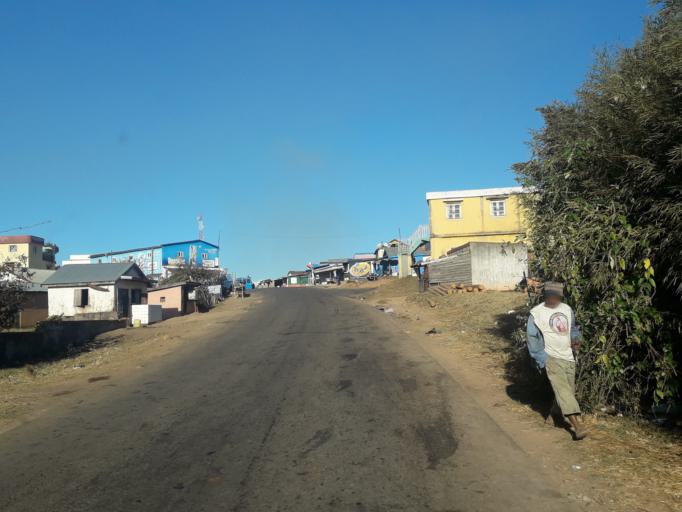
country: MG
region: Analamanga
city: Ankazobe
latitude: -18.0083
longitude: 47.1474
